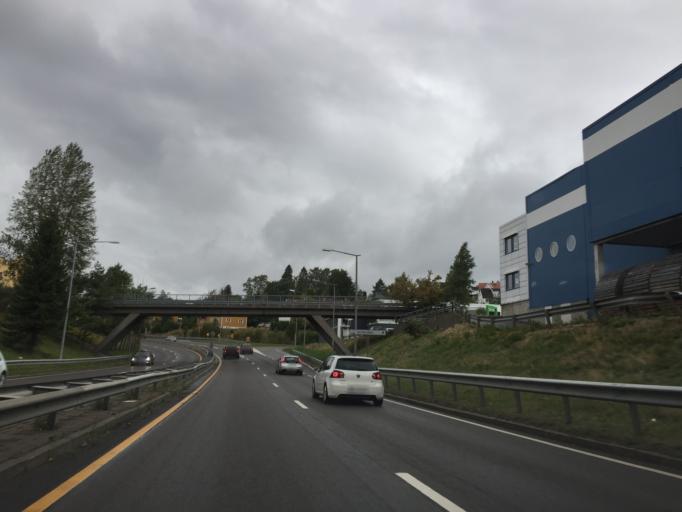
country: NO
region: Akershus
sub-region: Lorenskog
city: Kjenn
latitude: 59.9547
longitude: 10.8967
